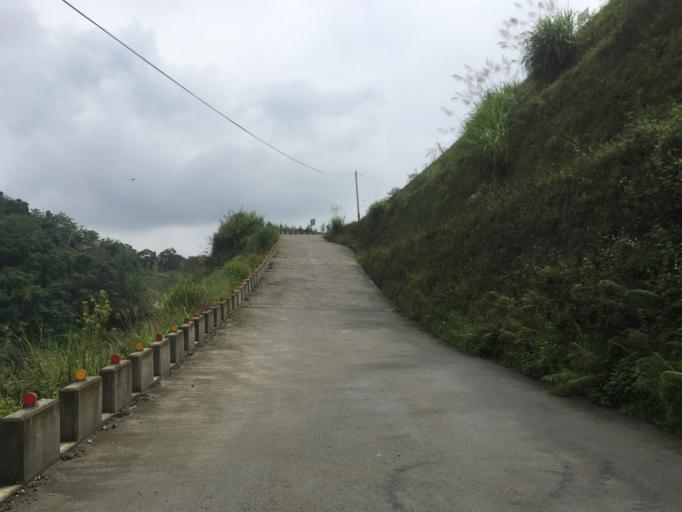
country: TW
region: Taiwan
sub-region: Taichung City
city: Taichung
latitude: 24.1716
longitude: 120.7763
